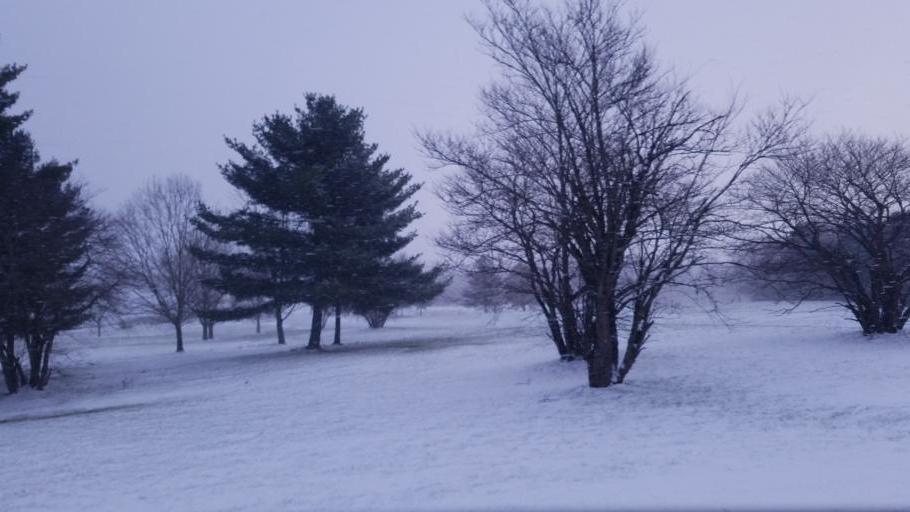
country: US
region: Ohio
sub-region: Knox County
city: Fredericktown
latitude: 40.5018
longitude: -82.5788
